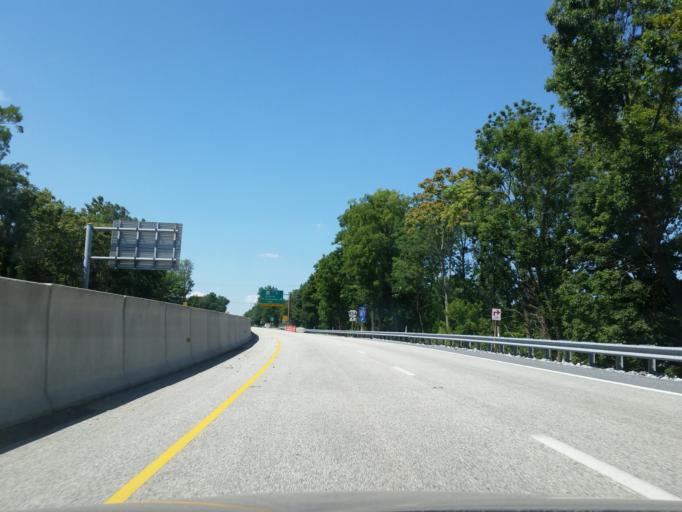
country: US
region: Pennsylvania
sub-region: Lebanon County
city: Palmyra
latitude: 40.4076
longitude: -76.5782
